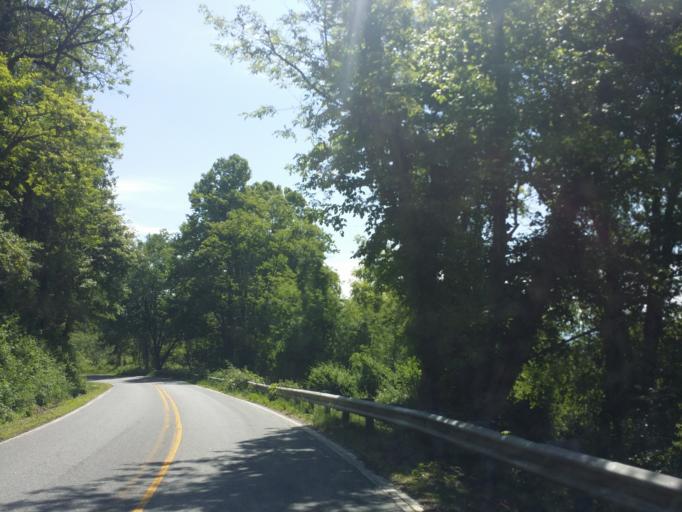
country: US
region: North Carolina
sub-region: Madison County
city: Marshall
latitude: 35.7112
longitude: -82.8321
